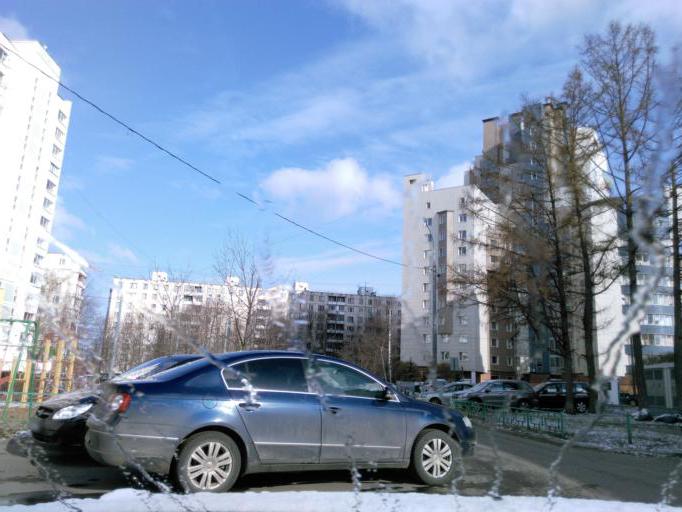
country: RU
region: Moskovskaya
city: Mendeleyevo
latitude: 56.0056
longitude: 37.2028
